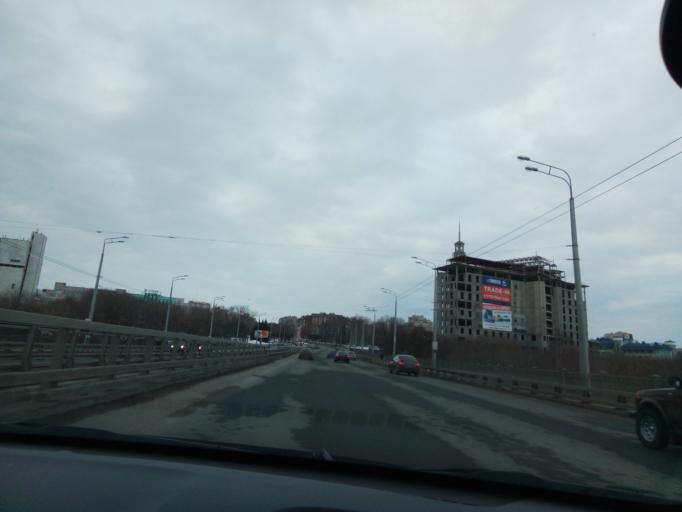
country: RU
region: Chuvashia
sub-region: Cheboksarskiy Rayon
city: Cheboksary
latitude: 56.1450
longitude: 47.2424
